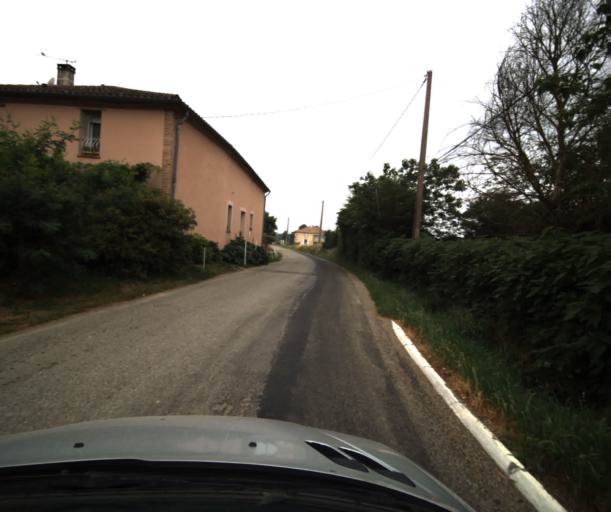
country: FR
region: Midi-Pyrenees
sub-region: Departement du Tarn-et-Garonne
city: Saint-Nicolas-de-la-Grave
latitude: 44.0711
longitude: 0.9912
